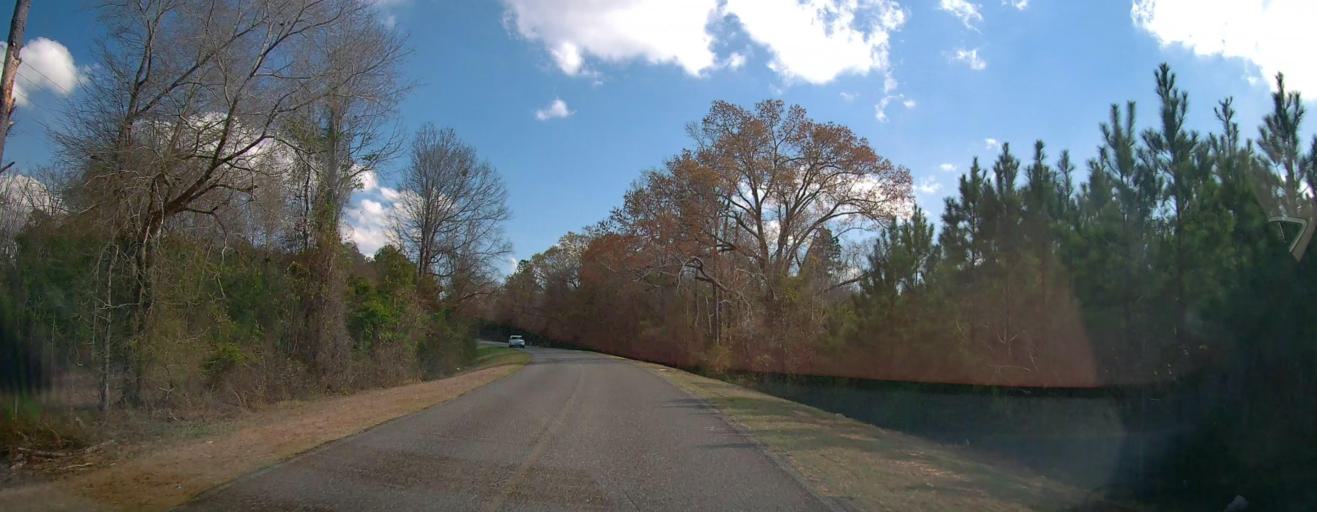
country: US
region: Georgia
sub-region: Twiggs County
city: Jeffersonville
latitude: 32.6669
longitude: -83.2334
